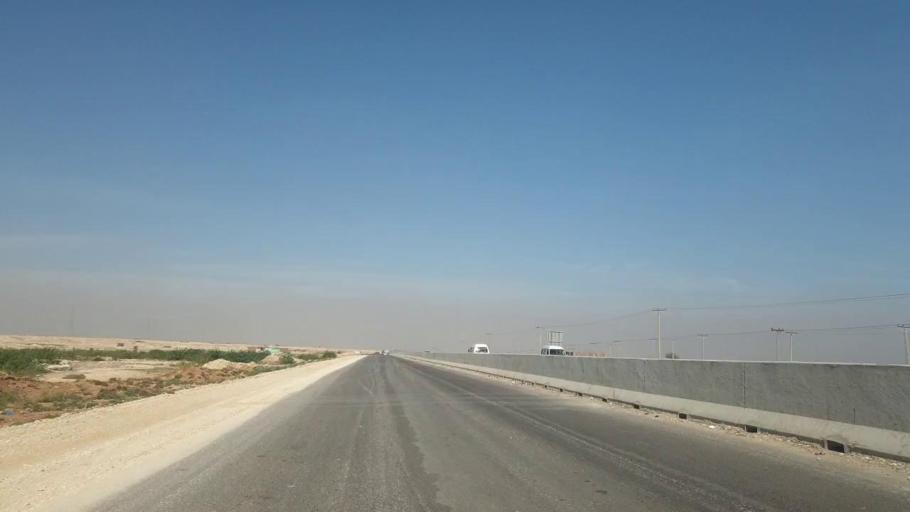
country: PK
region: Sindh
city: Jamshoro
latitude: 25.4870
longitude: 68.2720
